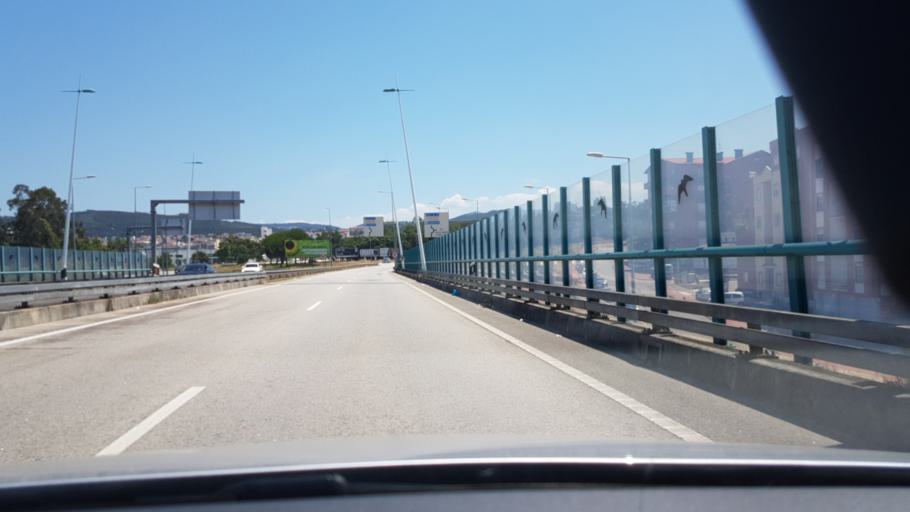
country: PT
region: Coimbra
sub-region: Coimbra
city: Coimbra
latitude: 40.1926
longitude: -8.4187
